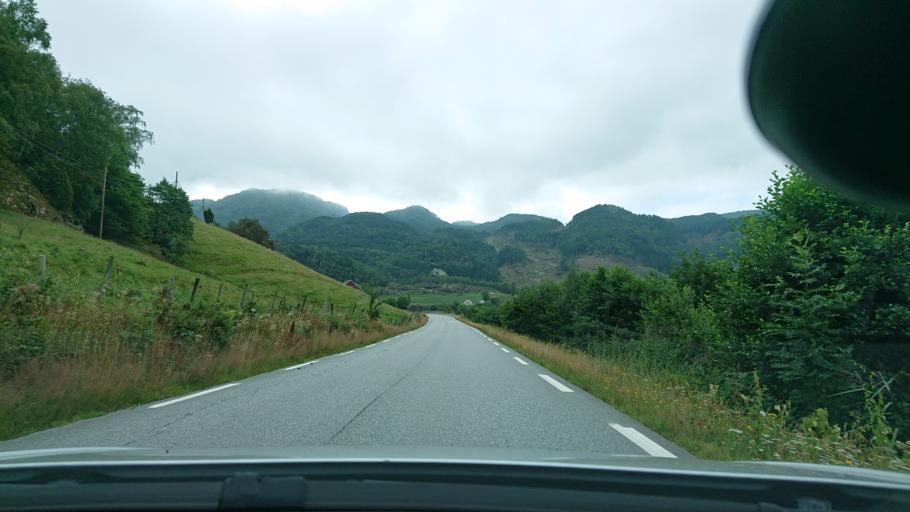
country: NO
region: Rogaland
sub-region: Hjelmeland
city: Hjelmelandsvagen
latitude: 59.2302
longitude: 6.2047
